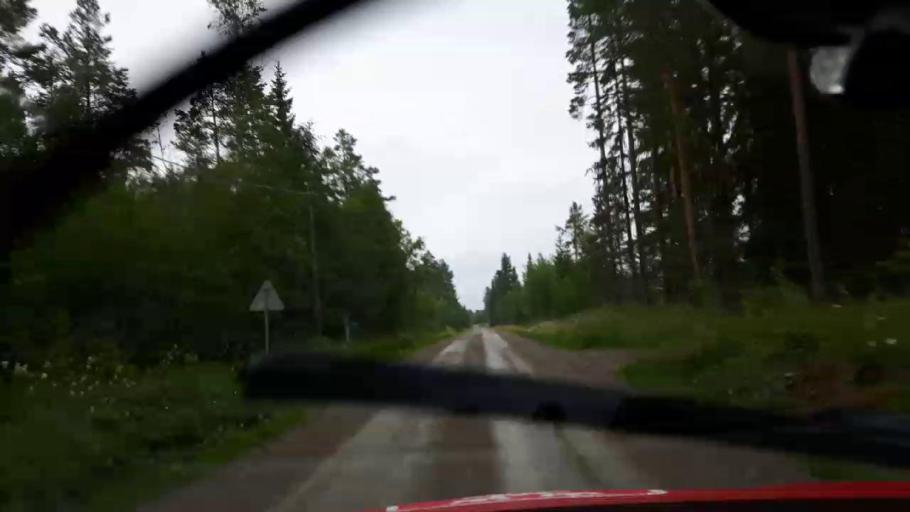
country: SE
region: Jaemtland
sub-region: OEstersunds Kommun
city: Brunflo
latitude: 62.8167
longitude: 14.9222
